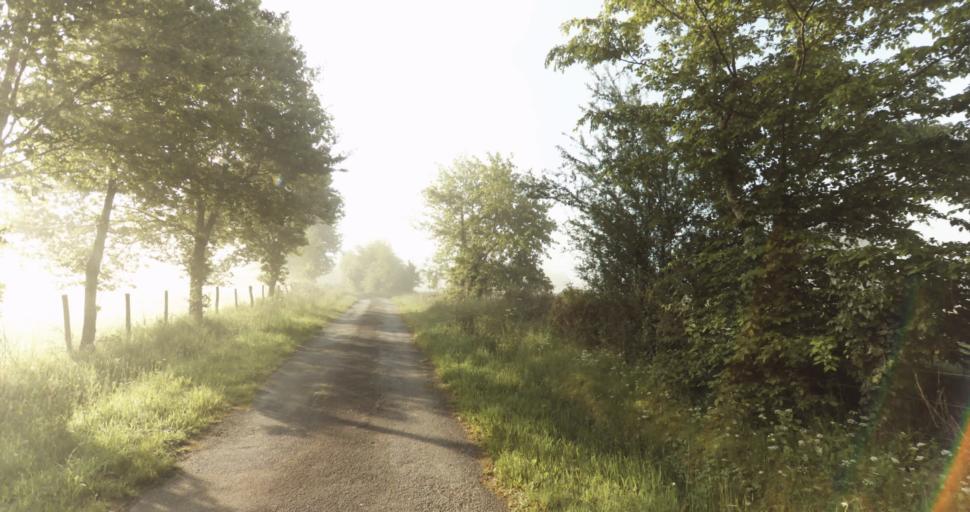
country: FR
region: Limousin
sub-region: Departement de la Haute-Vienne
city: Condat-sur-Vienne
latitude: 45.7859
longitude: 1.2812
